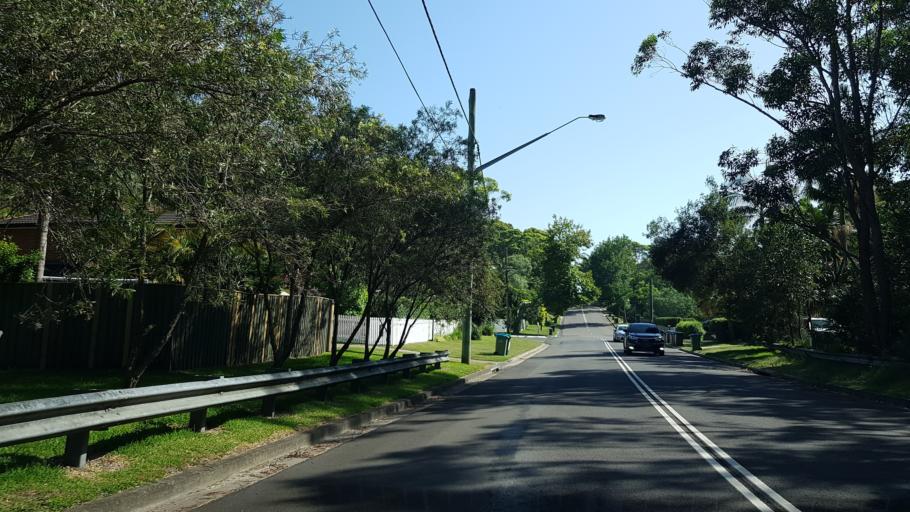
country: AU
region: New South Wales
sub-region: Warringah
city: Narraweena
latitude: -33.7408
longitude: 151.2682
